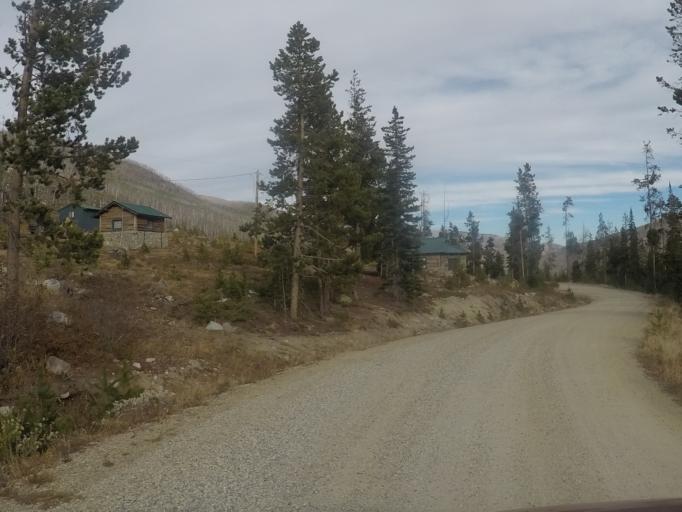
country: US
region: Montana
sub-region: Carbon County
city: Red Lodge
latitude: 45.1717
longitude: -109.4789
